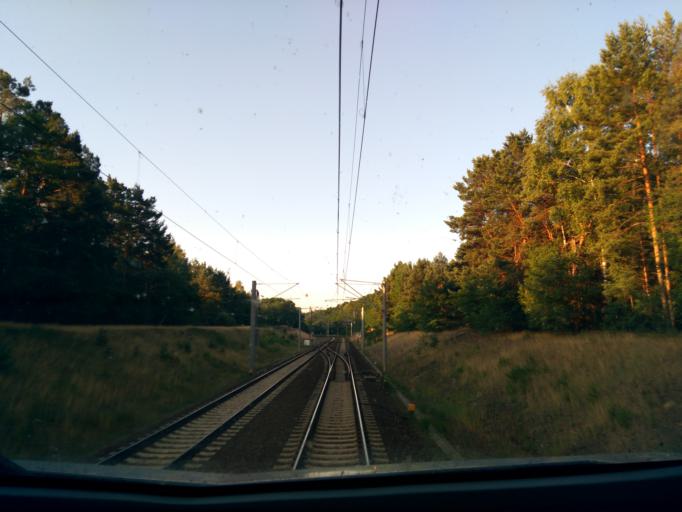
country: DE
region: Brandenburg
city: Halbe
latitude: 52.0396
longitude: 13.7189
